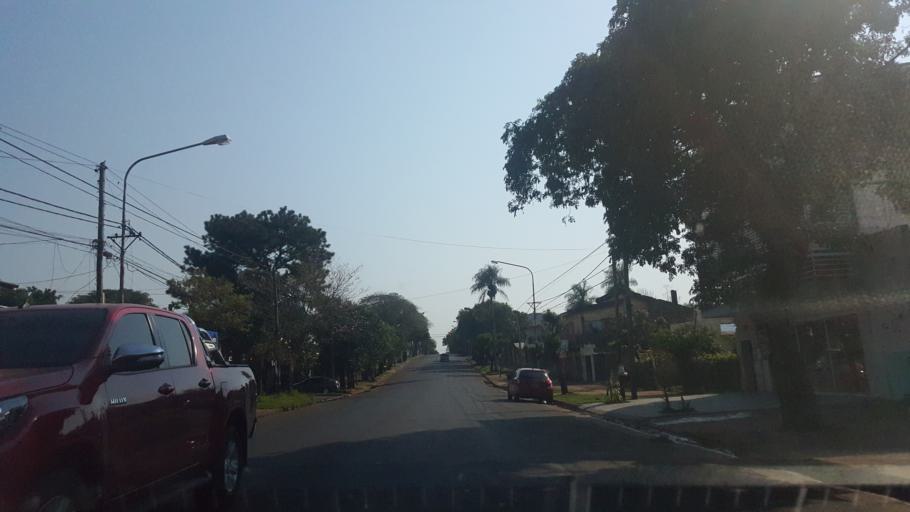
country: AR
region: Misiones
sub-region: Departamento de Capital
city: Posadas
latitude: -27.3818
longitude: -55.9071
